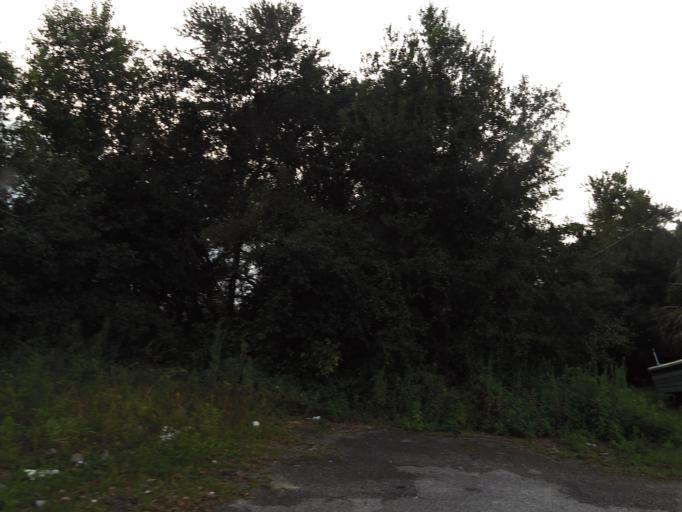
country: US
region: Florida
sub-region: Duval County
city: Jacksonville
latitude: 30.3480
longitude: -81.7024
